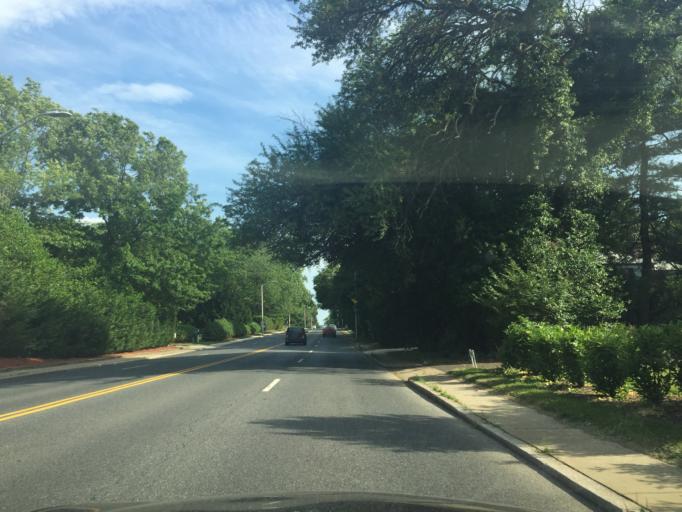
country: US
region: Maryland
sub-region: Baltimore County
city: Towson
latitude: 39.3677
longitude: -76.6257
